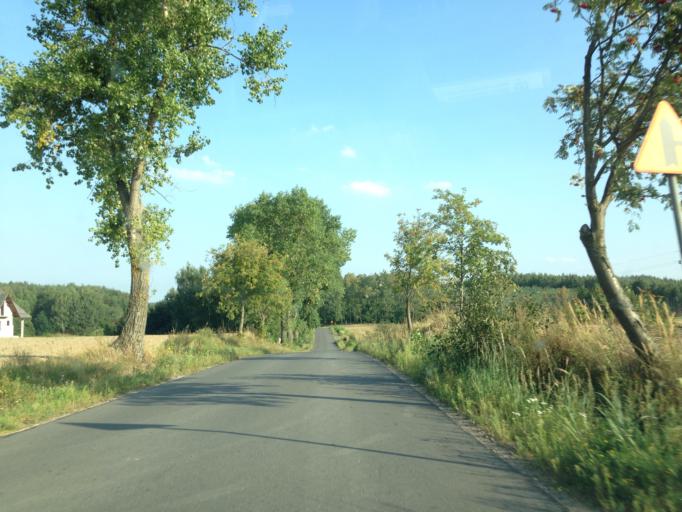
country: PL
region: Warmian-Masurian Voivodeship
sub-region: Powiat nowomiejski
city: Biskupiec
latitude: 53.4208
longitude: 19.3177
